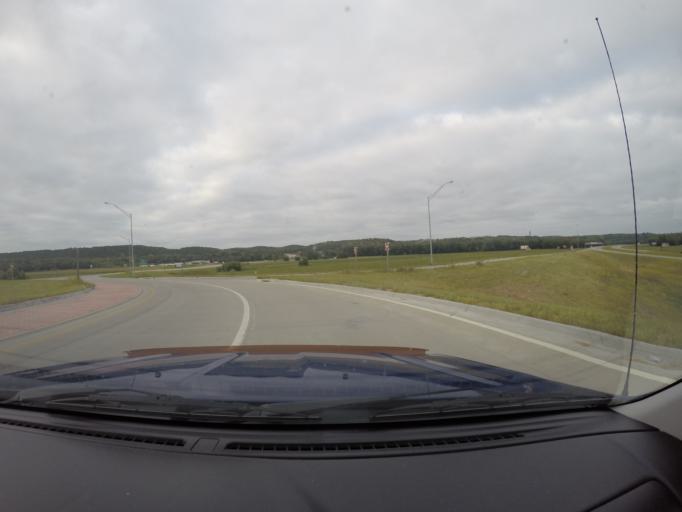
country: US
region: Kansas
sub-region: Riley County
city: Ogden
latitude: 39.1553
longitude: -96.6438
